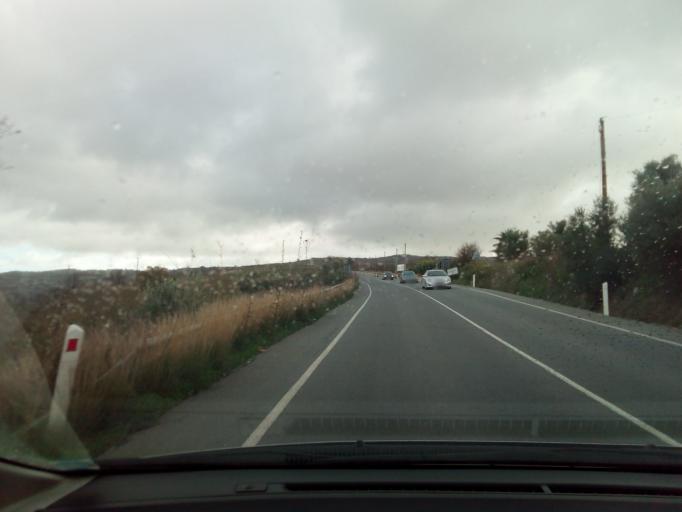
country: CY
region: Pafos
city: Tala
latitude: 34.9166
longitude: 32.4679
